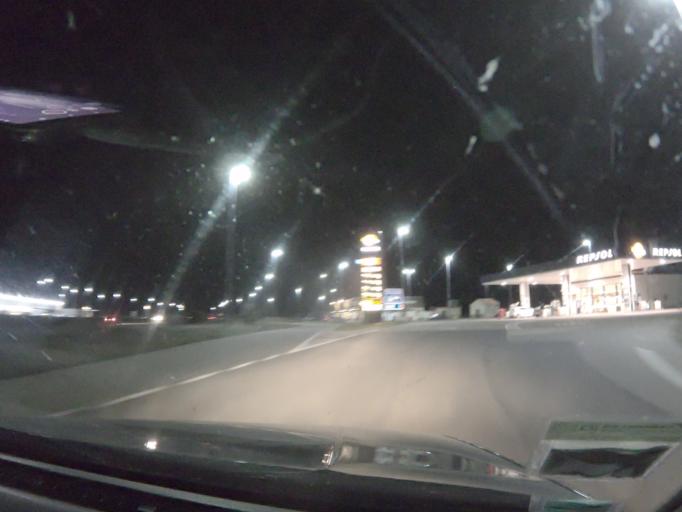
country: ES
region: Castille and Leon
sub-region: Provincia de Zamora
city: Pobladura del Valle
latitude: 42.0897
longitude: -5.7153
